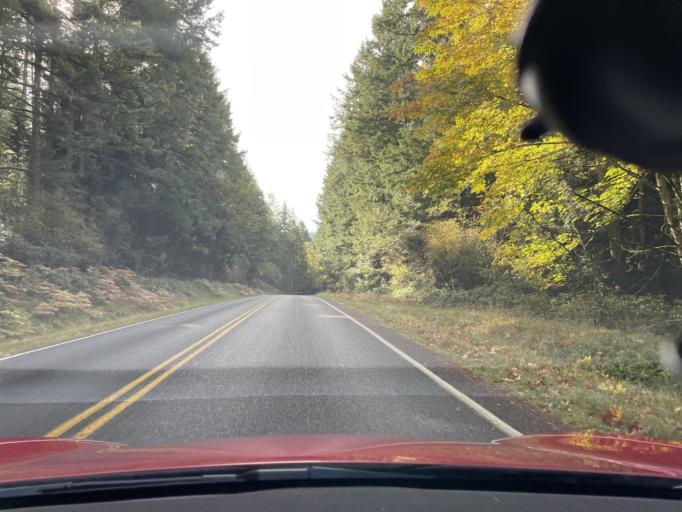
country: US
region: Washington
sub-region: San Juan County
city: Friday Harbor
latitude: 48.5964
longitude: -123.1327
